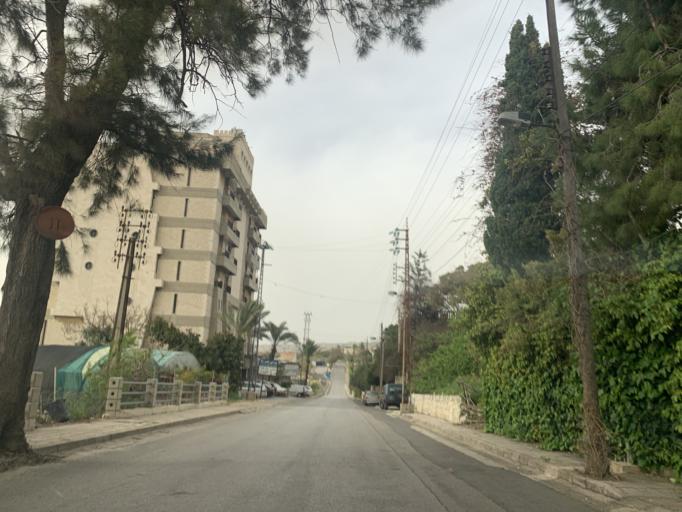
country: LB
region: Mont-Liban
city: Jbail
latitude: 34.1003
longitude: 35.6514
